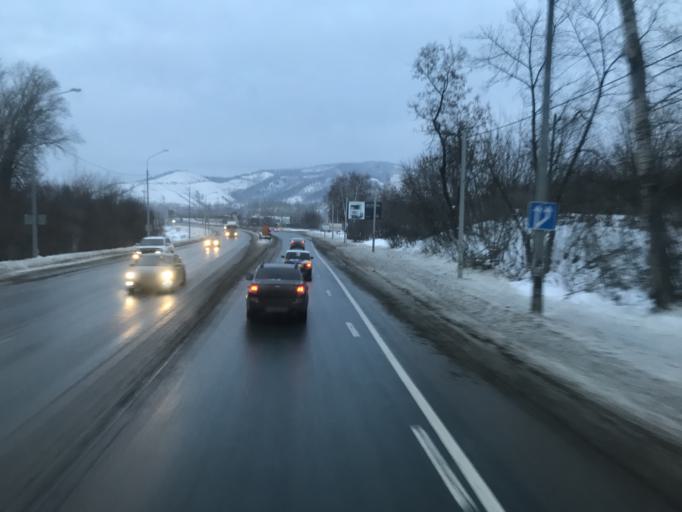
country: RU
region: Samara
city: Zhigulevsk
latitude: 53.4032
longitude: 49.4731
